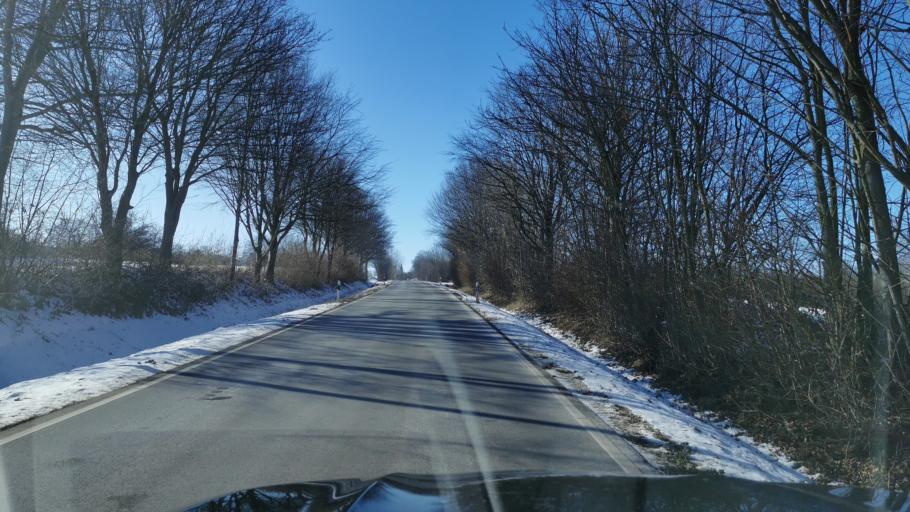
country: DE
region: Schleswig-Holstein
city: Westerholz
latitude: 54.8186
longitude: 9.6494
